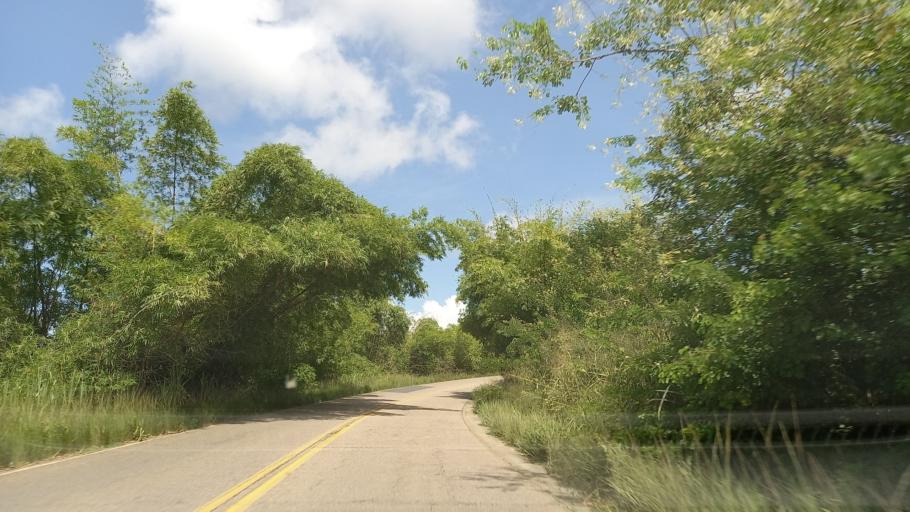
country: BR
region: Pernambuco
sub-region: Barreiros
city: Barreiros
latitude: -8.7644
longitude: -35.1685
